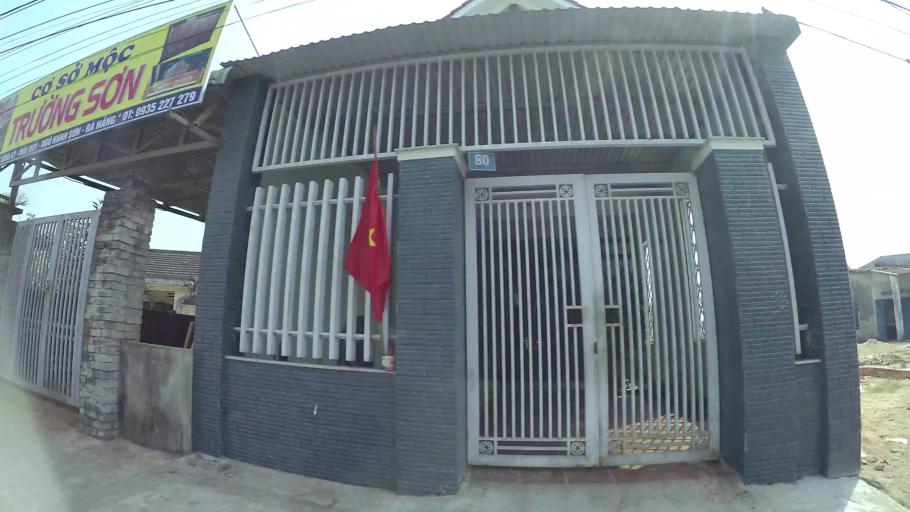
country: VN
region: Da Nang
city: Ngu Hanh Son
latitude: 15.9913
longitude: 108.2401
